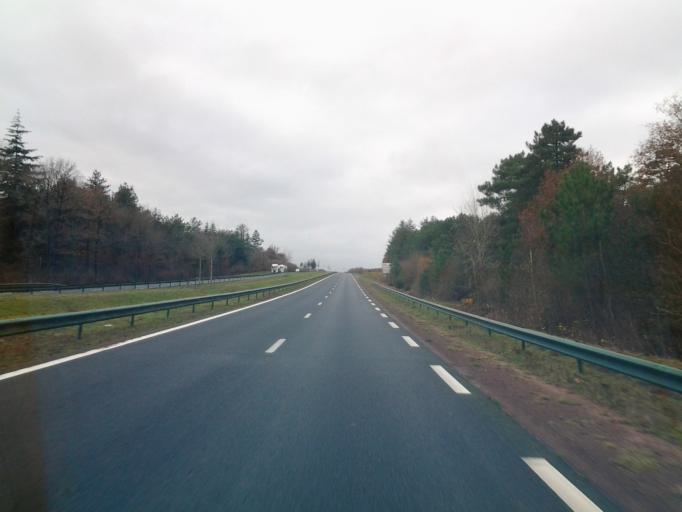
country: FR
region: Pays de la Loire
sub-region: Departement de la Vendee
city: Bournezeau
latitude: 46.6489
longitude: -1.2156
